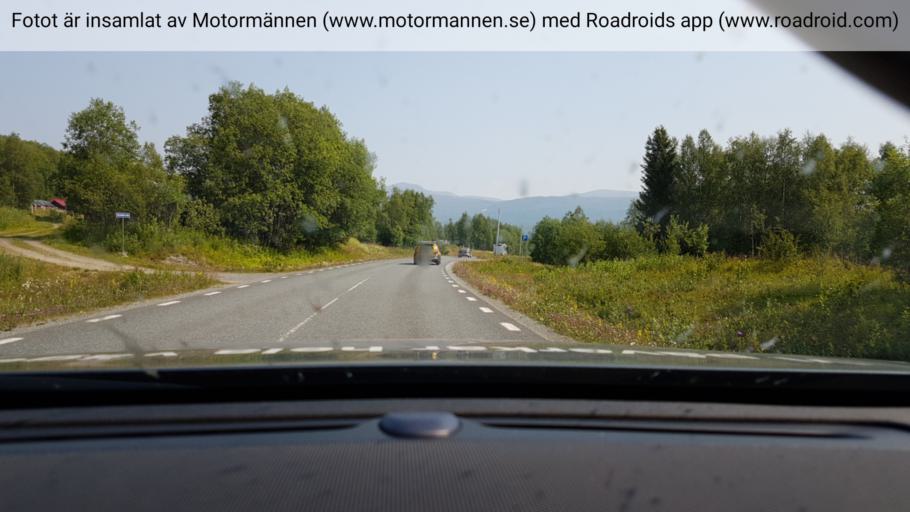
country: NO
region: Nordland
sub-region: Rana
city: Mo i Rana
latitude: 65.7484
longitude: 15.0930
